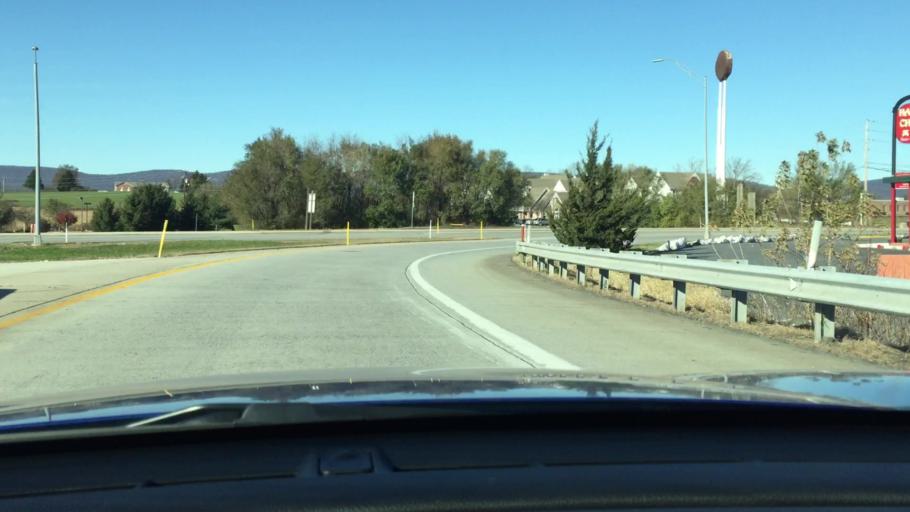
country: US
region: Pennsylvania
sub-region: Cumberland County
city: Schlusser
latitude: 40.2295
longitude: -77.1458
